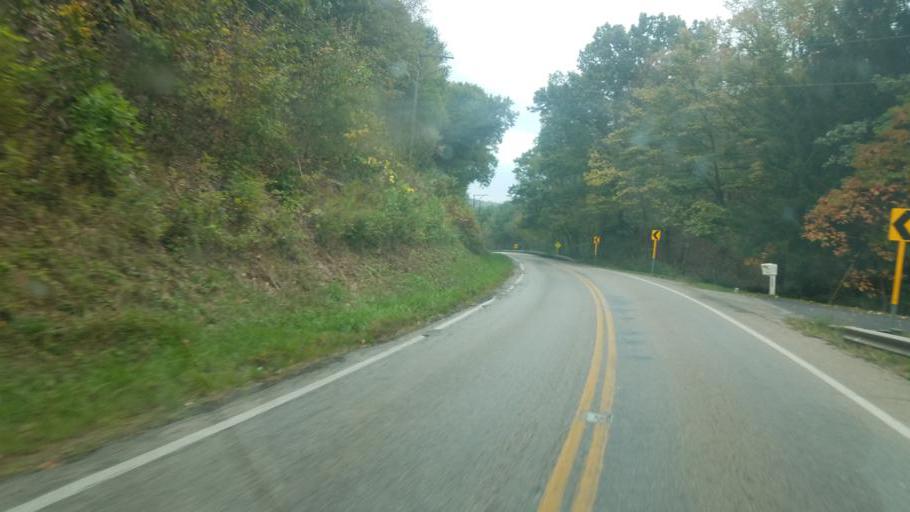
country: US
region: Ohio
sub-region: Ashland County
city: Loudonville
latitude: 40.6249
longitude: -82.1983
